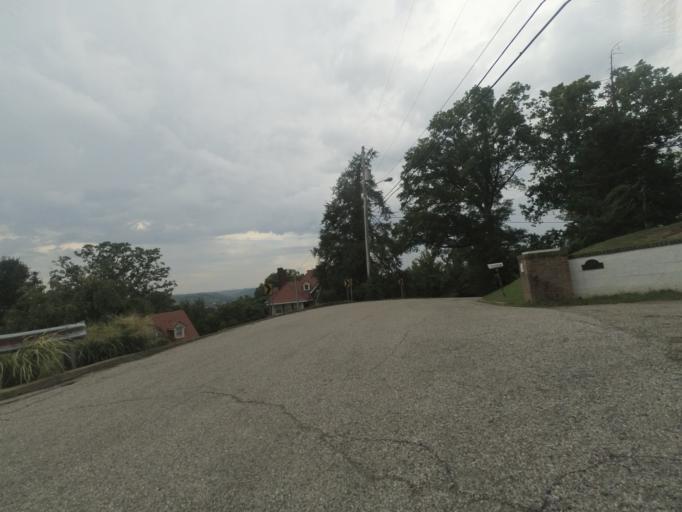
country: US
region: West Virginia
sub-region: Cabell County
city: Huntington
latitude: 38.4029
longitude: -82.4456
